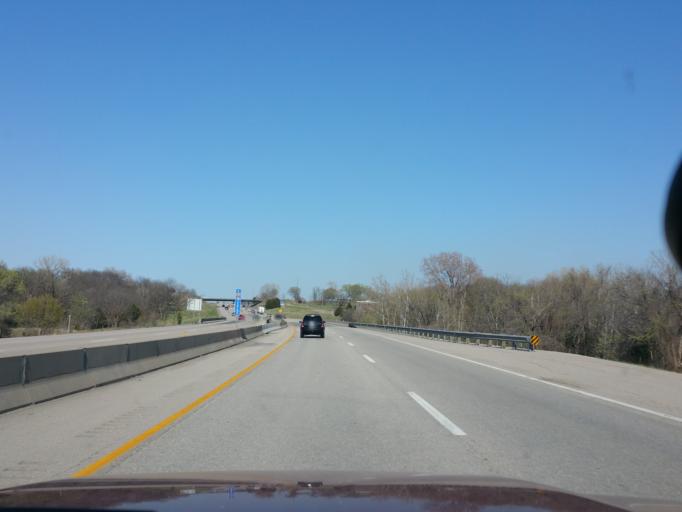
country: US
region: Kansas
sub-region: Douglas County
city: Lawrence
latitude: 38.9973
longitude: -95.1842
